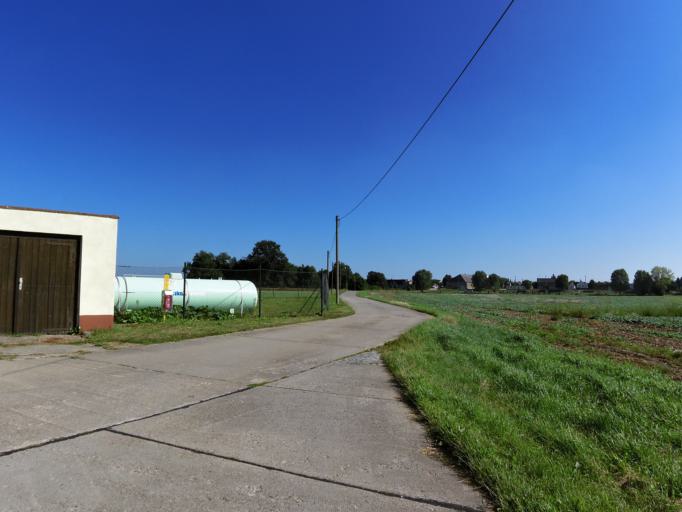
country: DE
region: Saxony
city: Riesa
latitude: 51.3206
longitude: 13.2943
